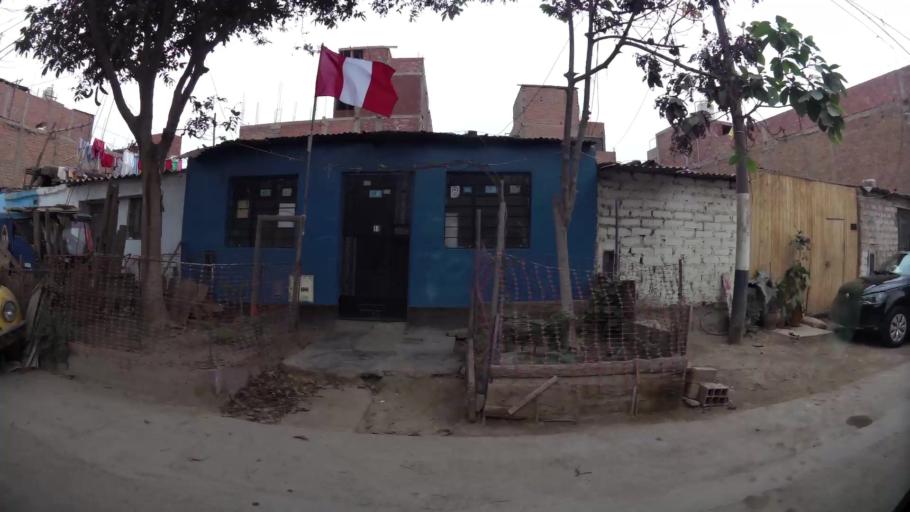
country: PE
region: Lima
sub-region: Lima
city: Independencia
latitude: -11.9610
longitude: -77.0813
